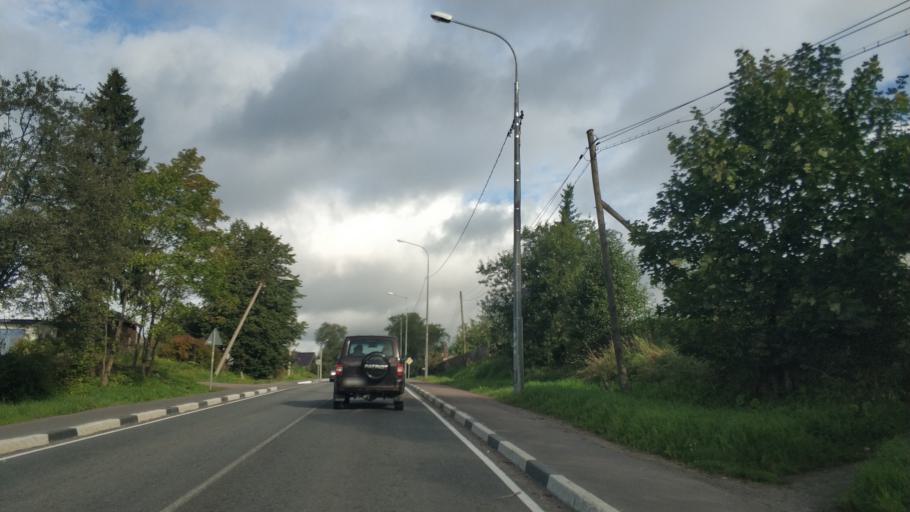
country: RU
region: Republic of Karelia
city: Khelyulya
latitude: 61.7490
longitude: 30.6644
